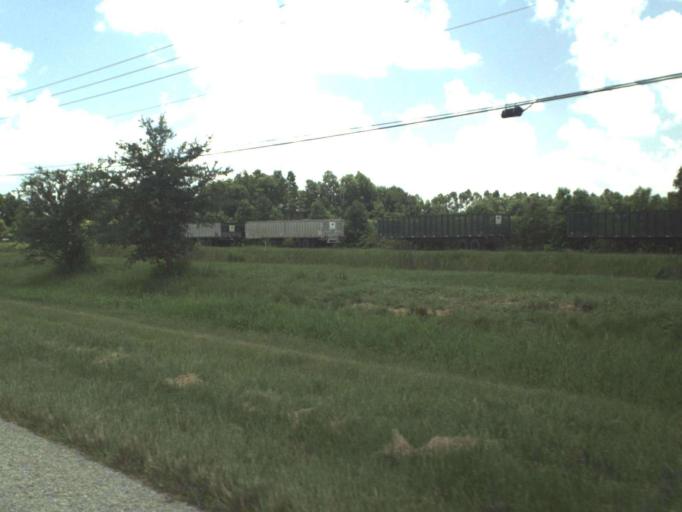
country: US
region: Florida
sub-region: Indian River County
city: Fellsmere
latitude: 27.6401
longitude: -80.6313
